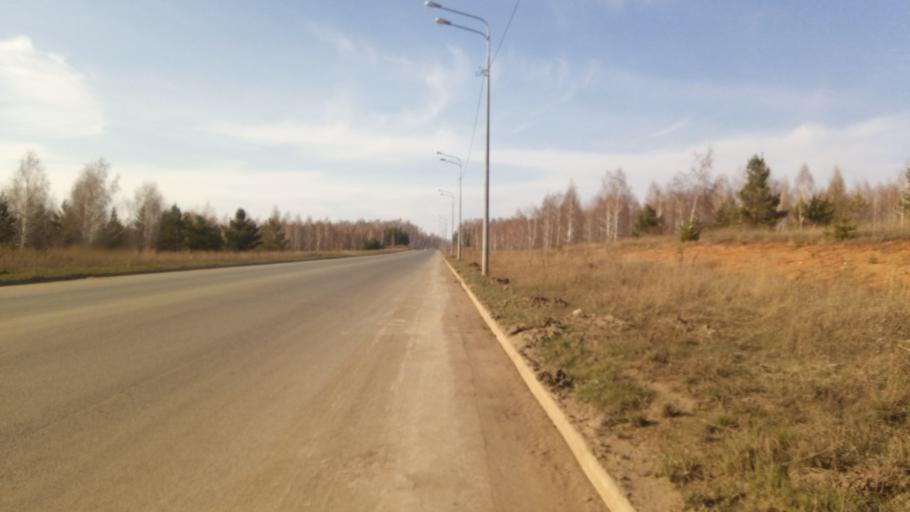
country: RU
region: Chelyabinsk
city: Sargazy
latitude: 55.1155
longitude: 61.2547
